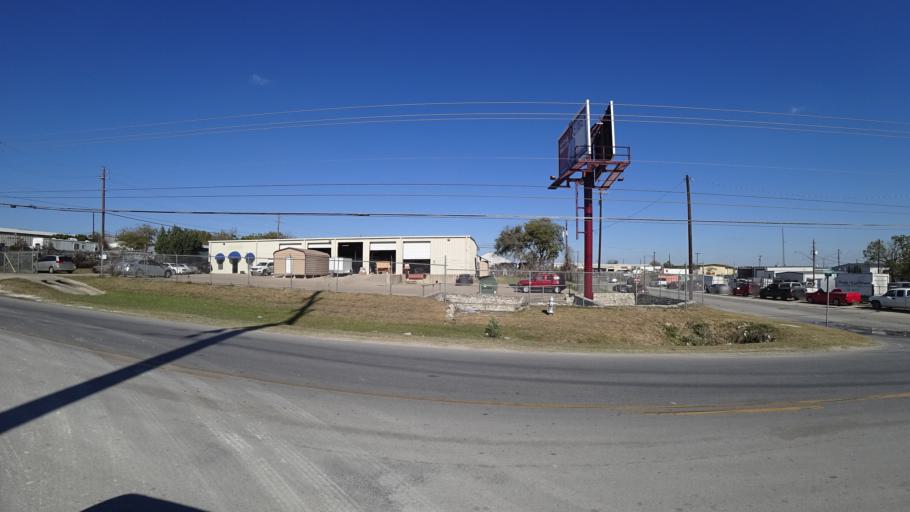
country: US
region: Texas
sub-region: Travis County
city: Wells Branch
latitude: 30.4293
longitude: -97.6817
